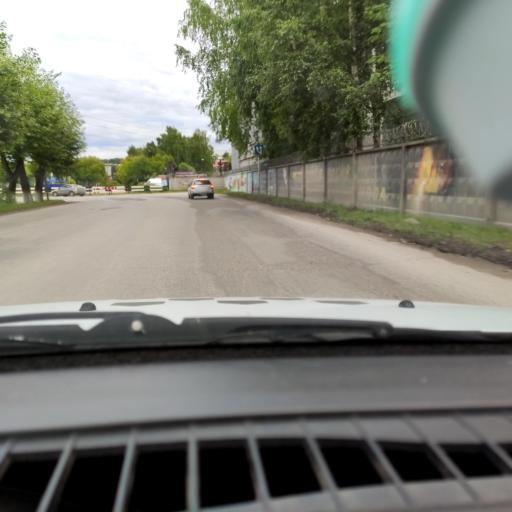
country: RU
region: Perm
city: Chusovoy
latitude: 58.2918
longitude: 57.8169
